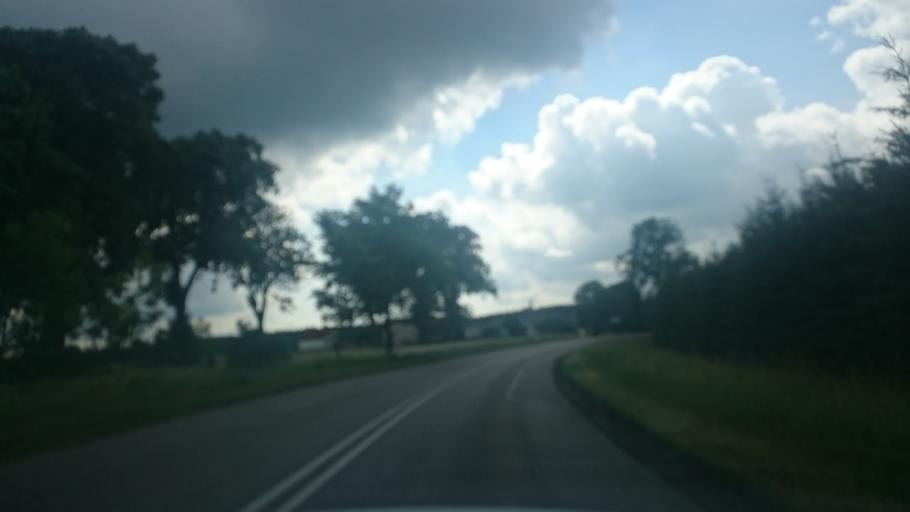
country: PL
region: Pomeranian Voivodeship
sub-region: Powiat koscierski
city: Stara Kiszewa
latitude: 53.9789
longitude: 18.2260
